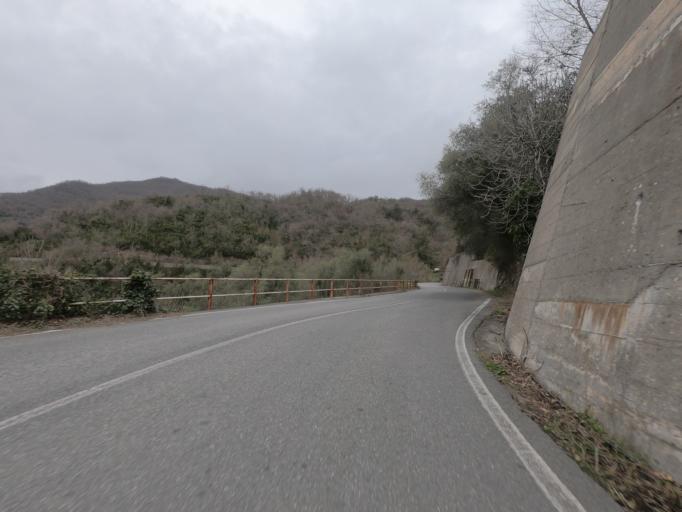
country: IT
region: Liguria
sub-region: Provincia di Savona
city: Casanova Lerrone
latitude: 44.0312
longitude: 8.0348
